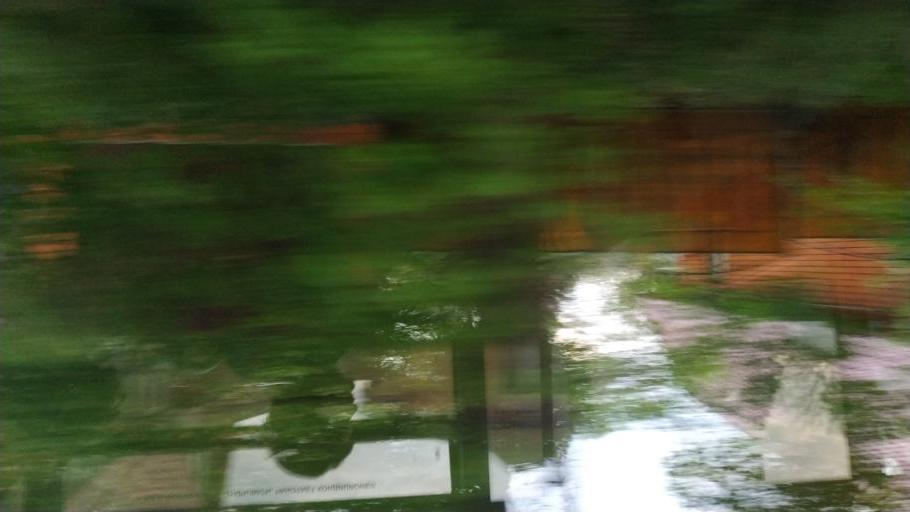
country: RU
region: Moskovskaya
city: Kashira
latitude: 54.8403
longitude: 38.1644
